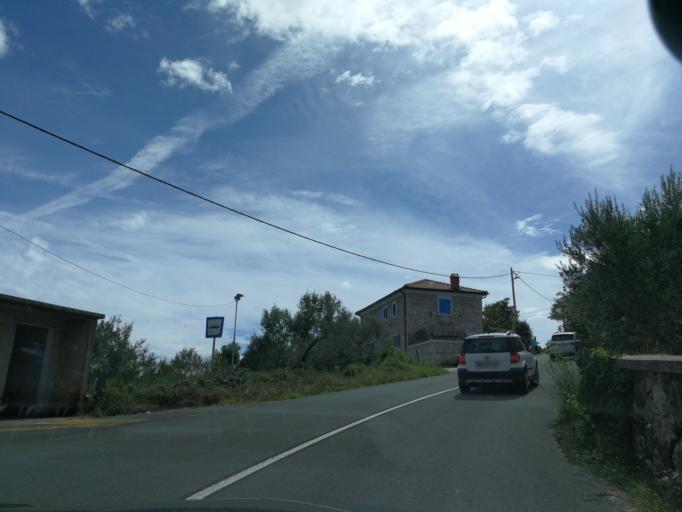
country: HR
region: Primorsko-Goranska
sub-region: Grad Crikvenica
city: Crikvenica
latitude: 45.1051
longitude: 14.6450
